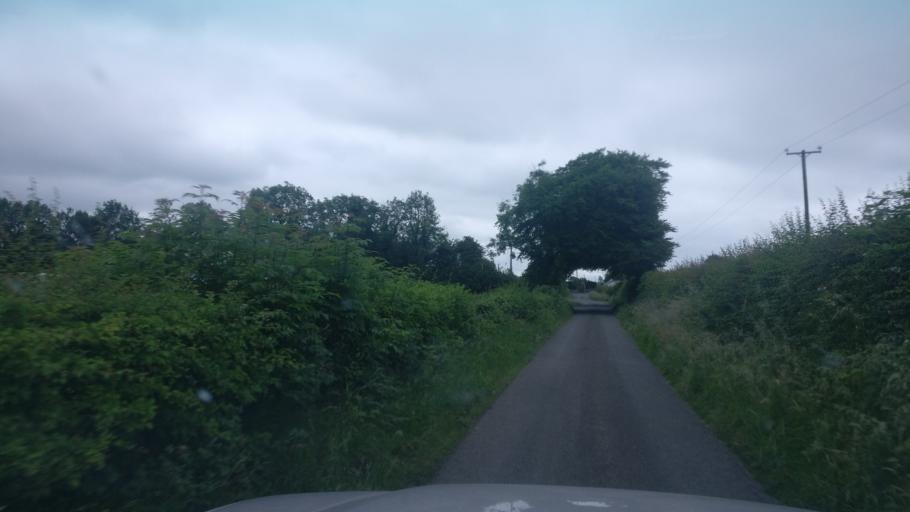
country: IE
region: Connaught
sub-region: County Galway
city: Ballinasloe
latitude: 53.2940
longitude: -8.3401
